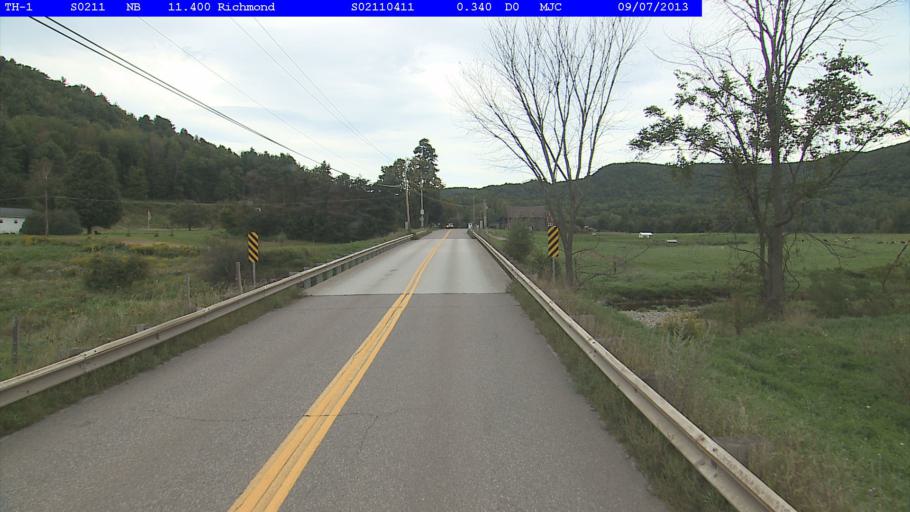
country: US
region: Vermont
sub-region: Chittenden County
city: Williston
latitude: 44.3581
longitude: -72.9930
